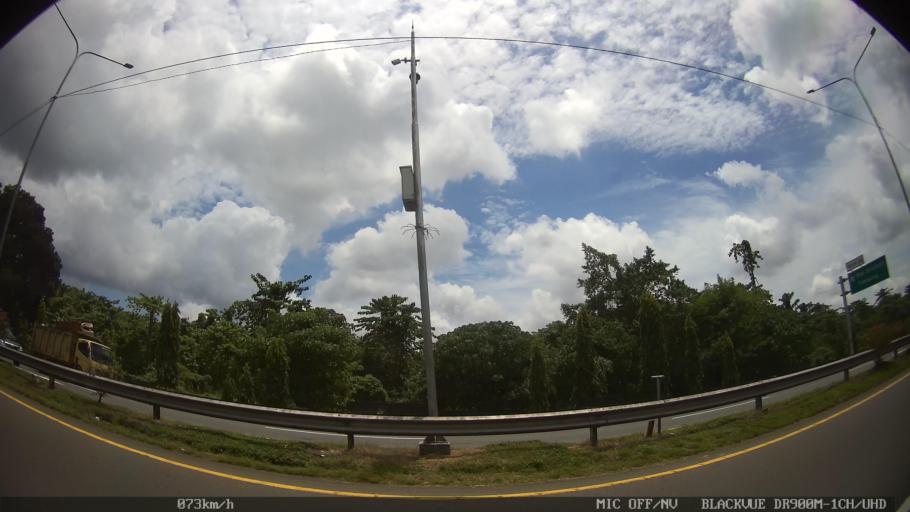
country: ID
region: North Sumatra
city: Medan
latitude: 3.6033
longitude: 98.7232
